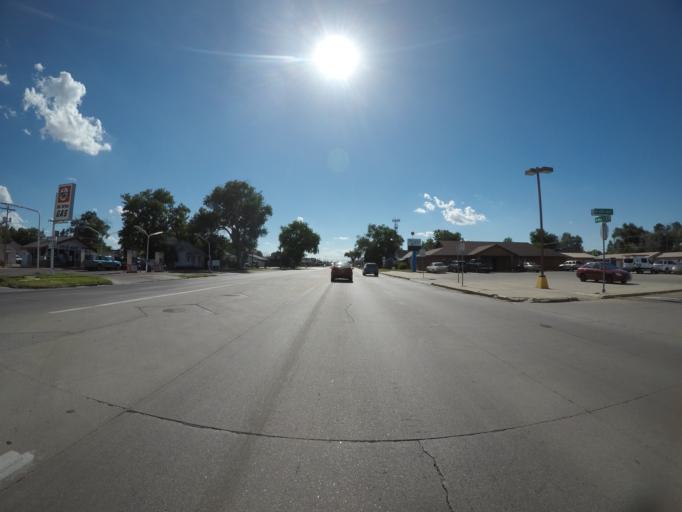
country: US
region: Colorado
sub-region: Logan County
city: Sterling
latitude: 40.6254
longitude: -103.2167
